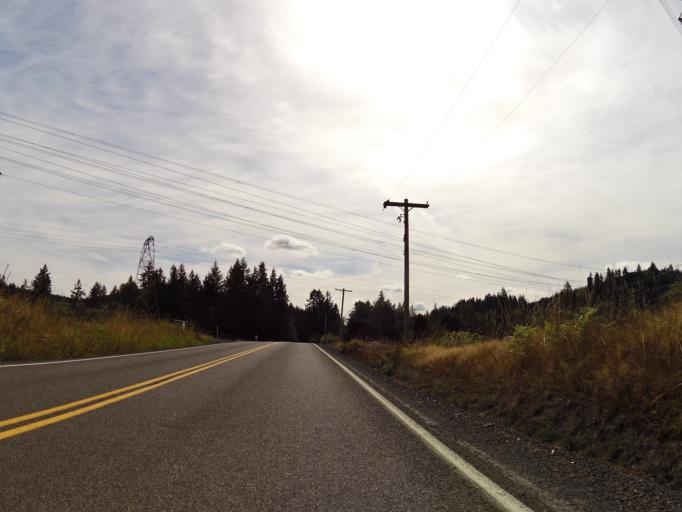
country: US
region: Washington
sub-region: Lewis County
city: Napavine
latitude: 46.5739
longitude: -122.9708
